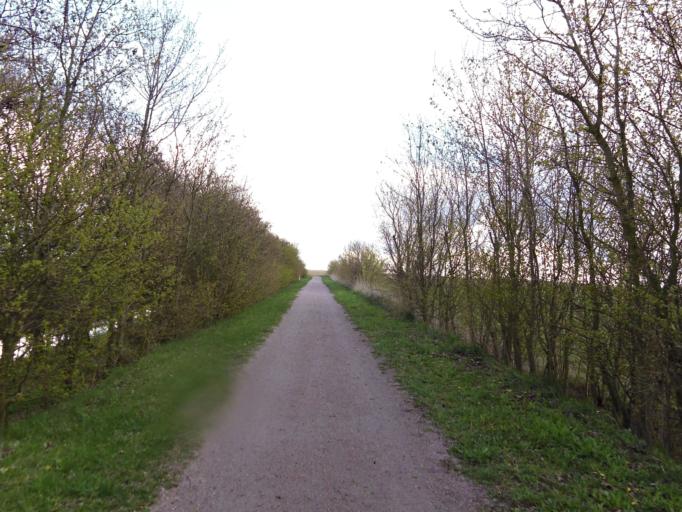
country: DE
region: Mecklenburg-Vorpommern
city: Saal
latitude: 54.3786
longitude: 12.4324
